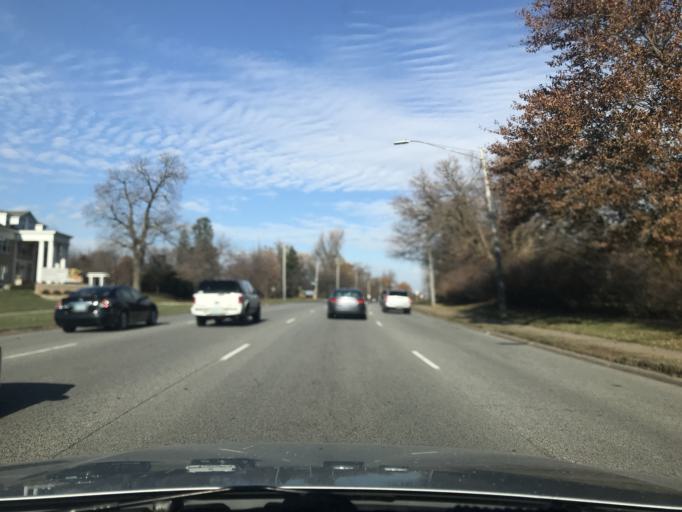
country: US
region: Iowa
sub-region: Scott County
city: Davenport
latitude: 41.5409
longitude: -90.5740
